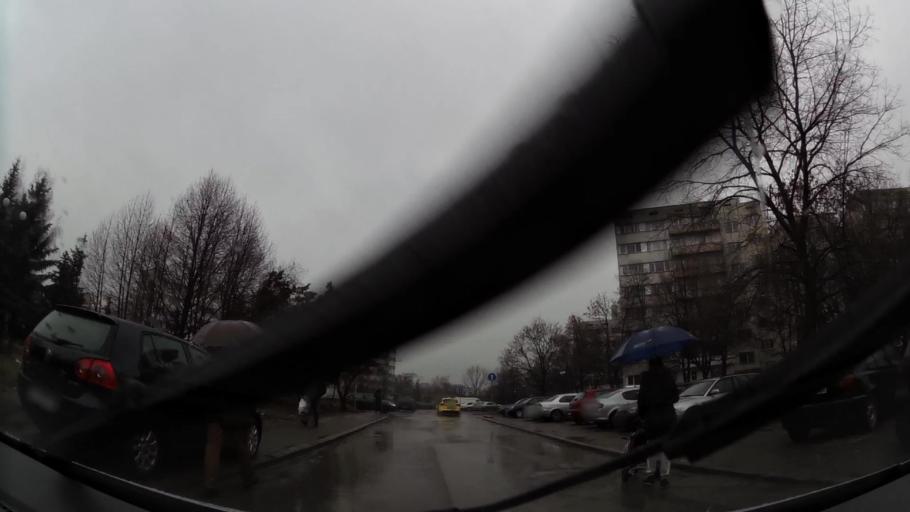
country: BG
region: Sofia-Capital
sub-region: Stolichna Obshtina
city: Sofia
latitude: 42.6478
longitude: 23.3389
